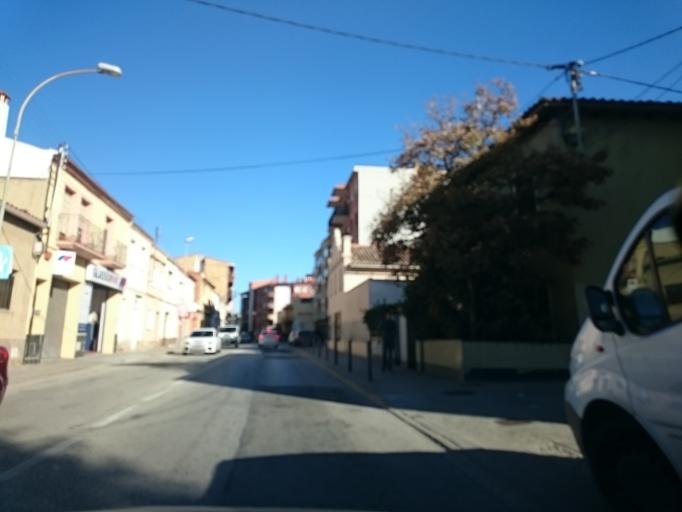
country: ES
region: Catalonia
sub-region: Provincia de Barcelona
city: Piera
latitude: 41.5239
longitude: 1.7508
